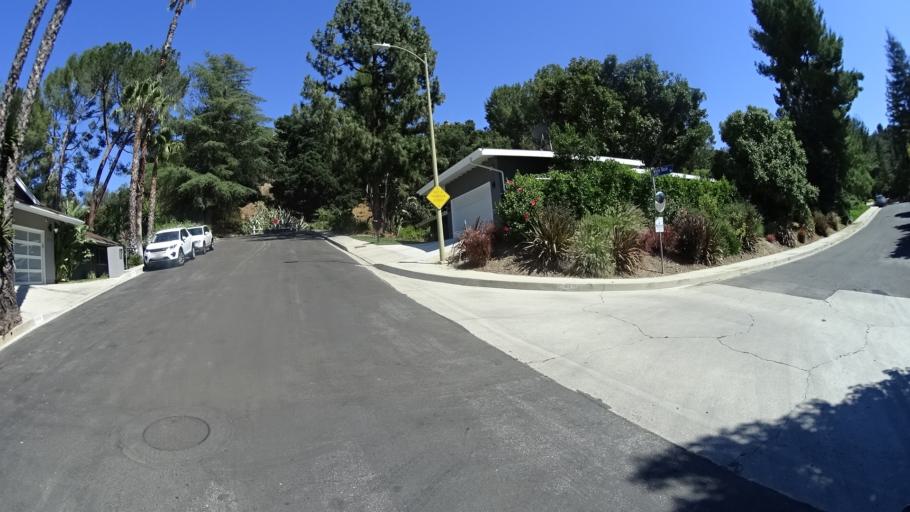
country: US
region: California
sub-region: Los Angeles County
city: Sherman Oaks
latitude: 34.1328
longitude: -118.4879
